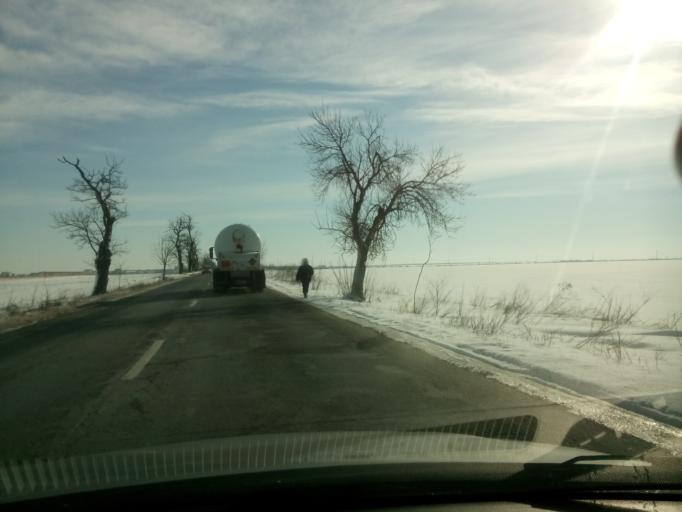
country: RO
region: Ilfov
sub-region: Comuna Glina
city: Glina
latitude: 44.3472
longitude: 26.2227
